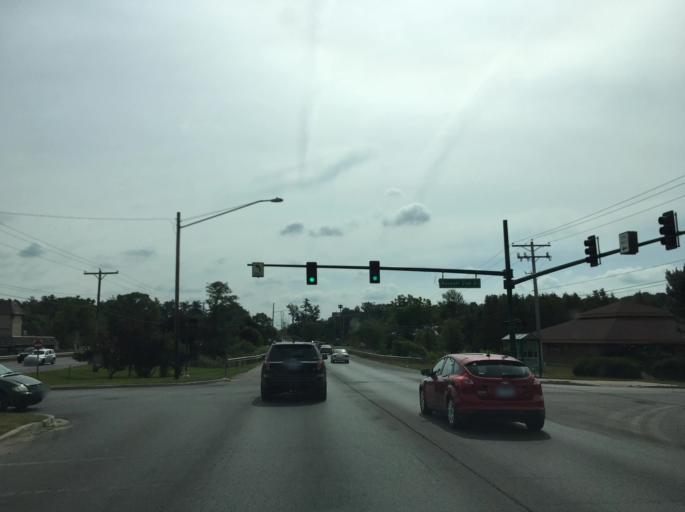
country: US
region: Michigan
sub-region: Grand Traverse County
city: Traverse City
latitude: 44.7333
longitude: -85.6178
